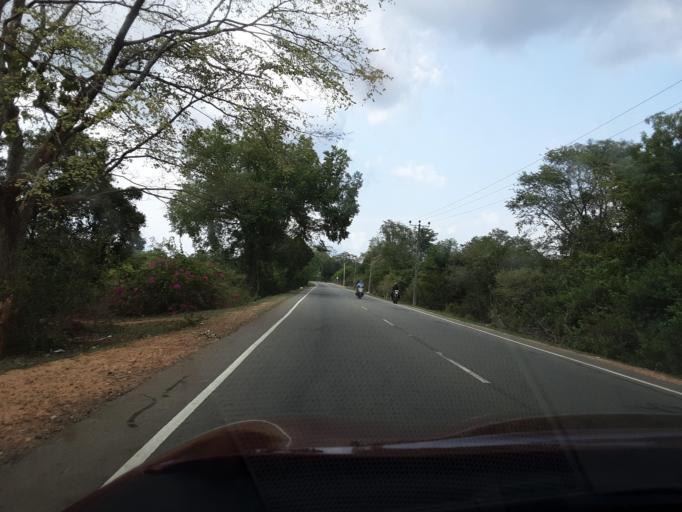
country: LK
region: Uva
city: Haputale
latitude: 6.5023
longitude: 81.1315
